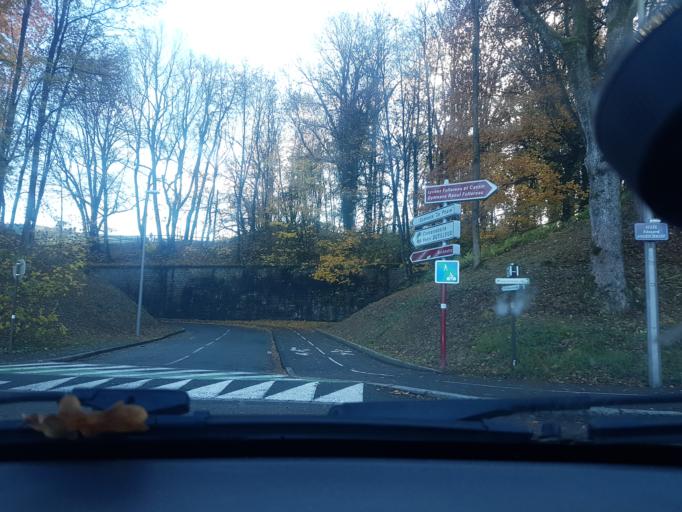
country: FR
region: Franche-Comte
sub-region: Territoire de Belfort
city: Belfort
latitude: 47.6401
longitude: 6.8488
